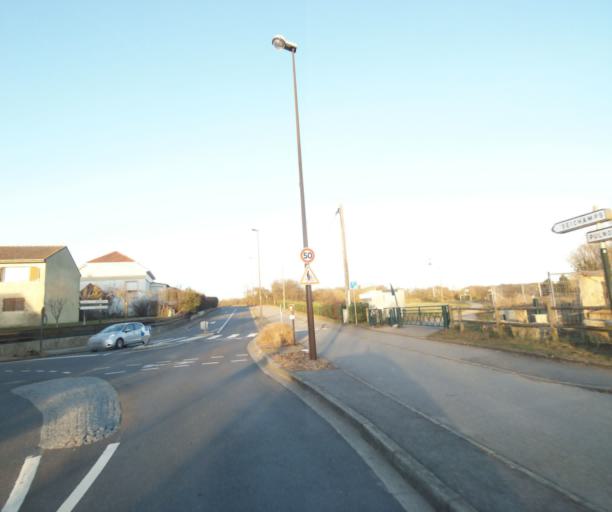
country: FR
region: Lorraine
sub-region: Departement de Meurthe-et-Moselle
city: Seichamps
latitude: 48.7071
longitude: 6.2620
